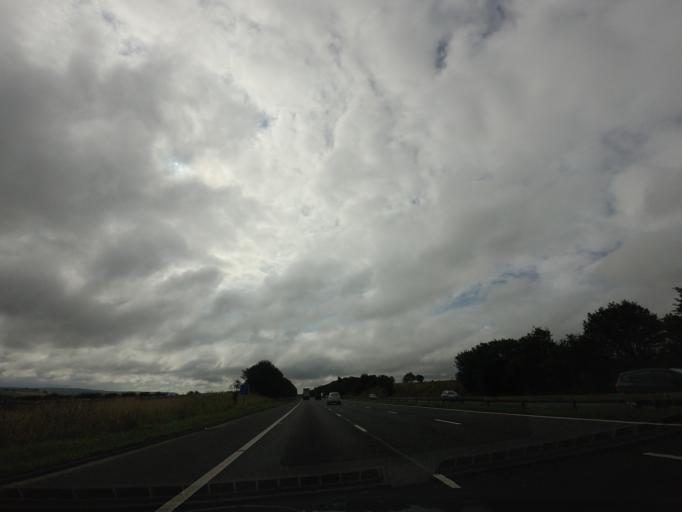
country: GB
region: England
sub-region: Cumbria
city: Scotby
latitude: 54.7749
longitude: -2.8494
